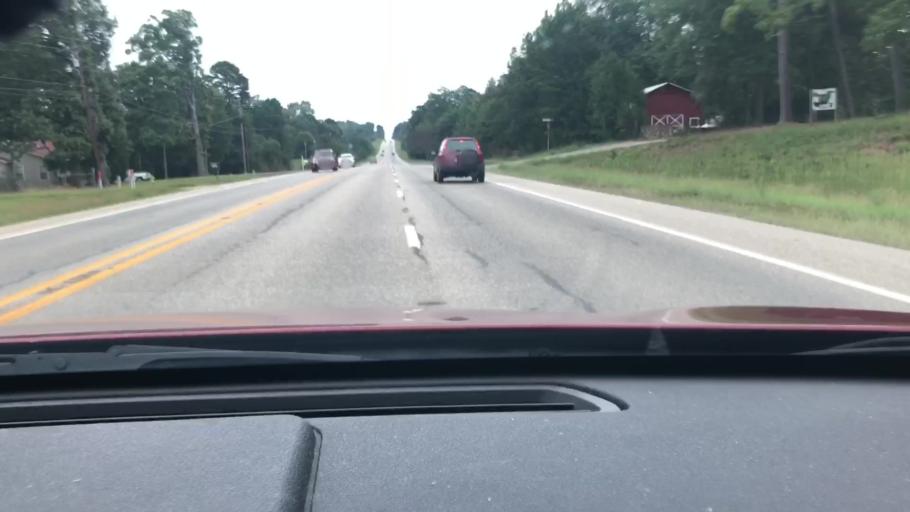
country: US
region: Arkansas
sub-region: Miller County
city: Texarkana
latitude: 33.4296
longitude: -93.9524
